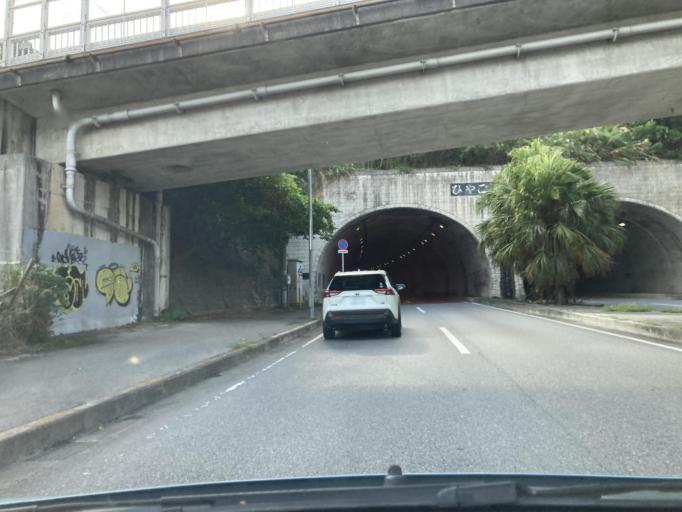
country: JP
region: Okinawa
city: Okinawa
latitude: 26.3178
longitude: 127.8129
